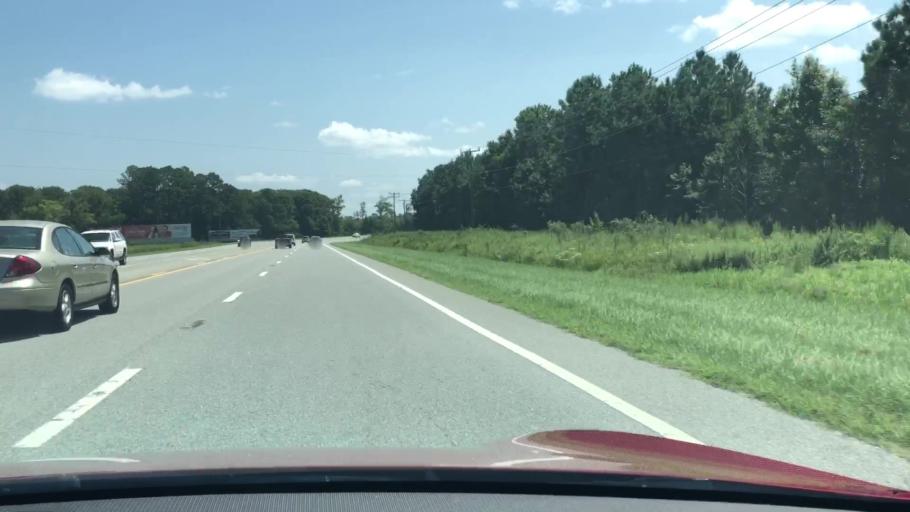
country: US
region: North Carolina
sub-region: Currituck County
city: Moyock
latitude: 36.4699
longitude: -76.1093
